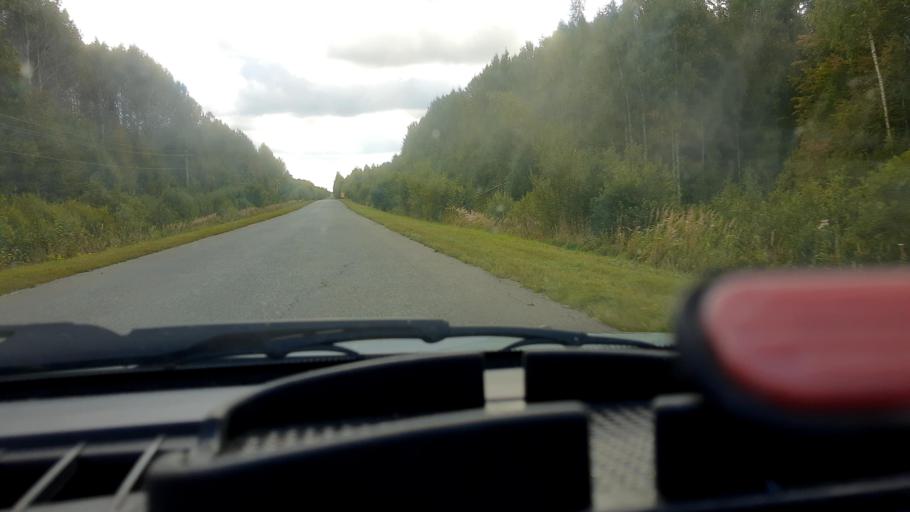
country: RU
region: Mariy-El
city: Kilemary
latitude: 56.9126
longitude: 46.7269
